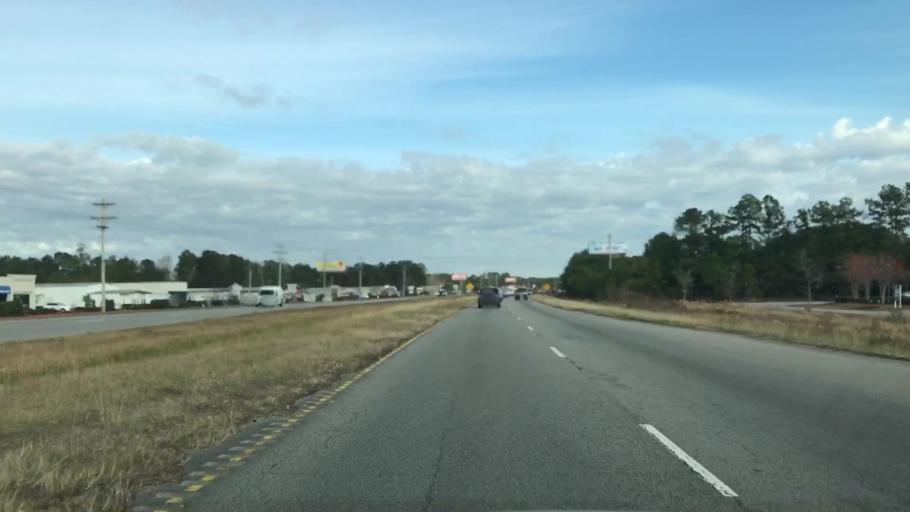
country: US
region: South Carolina
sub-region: Horry County
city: Garden City
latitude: 33.5888
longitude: -79.0265
